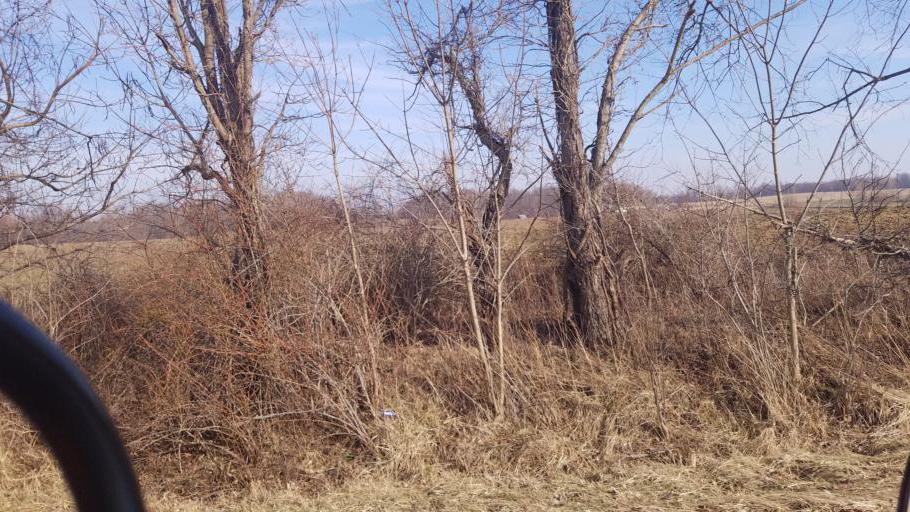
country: US
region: Ohio
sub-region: Richland County
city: Lexington
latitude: 40.6831
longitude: -82.6894
